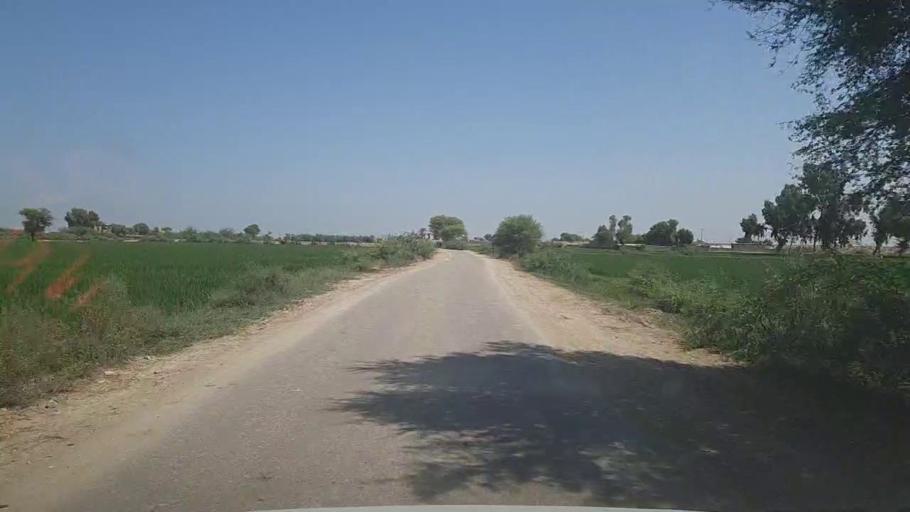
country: PK
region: Sindh
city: Kashmor
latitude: 28.2821
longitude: 69.4403
